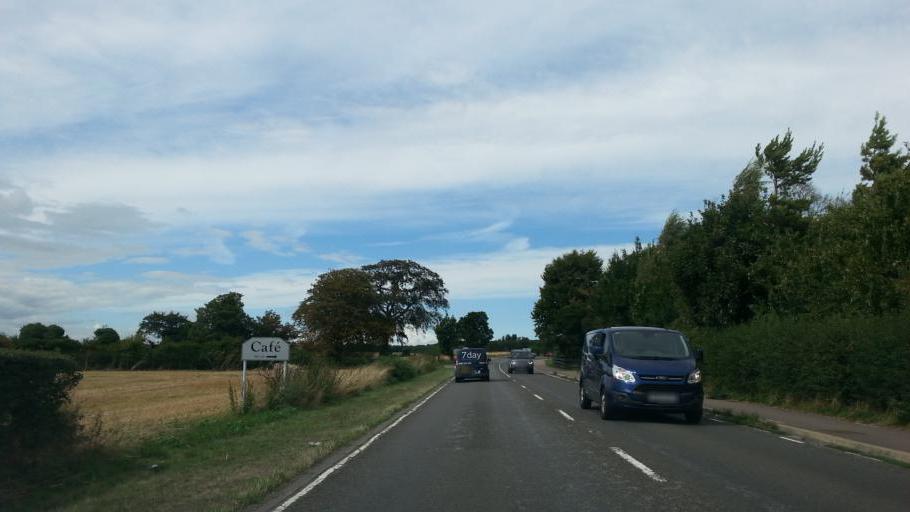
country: GB
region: England
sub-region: Cambridgeshire
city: Sawston
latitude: 52.1468
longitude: 0.1936
